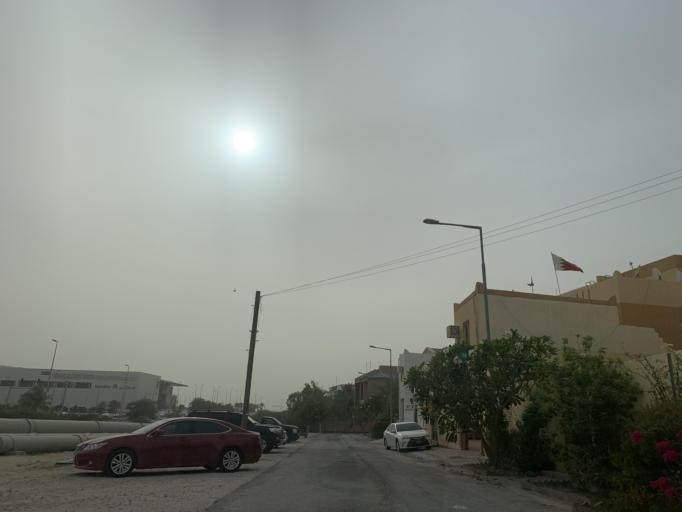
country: BH
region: Central Governorate
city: Madinat Hamad
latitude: 26.1381
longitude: 50.5230
